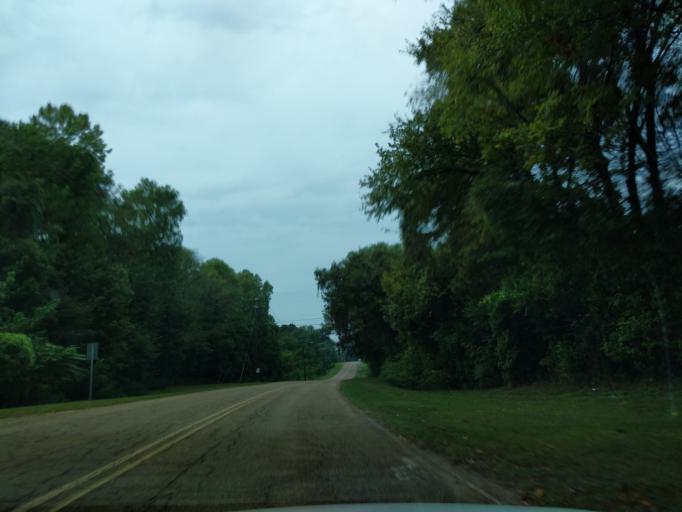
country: US
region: Mississippi
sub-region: Warren County
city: Vicksburg
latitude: 32.3166
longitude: -90.8850
